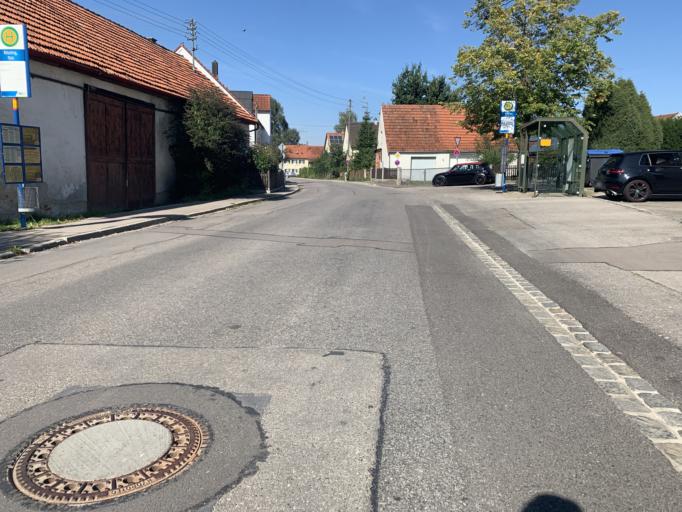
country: DE
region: Bavaria
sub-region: Swabia
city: Kissing
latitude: 48.2975
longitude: 10.9879
